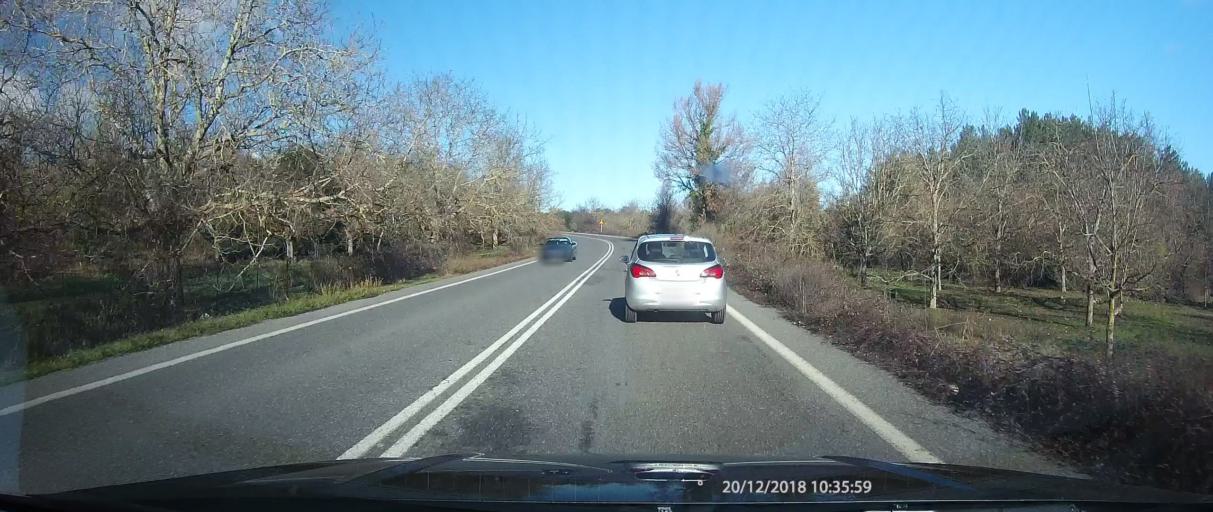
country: GR
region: Peloponnese
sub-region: Nomos Lakonias
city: Kariai
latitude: 37.3610
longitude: 22.4048
